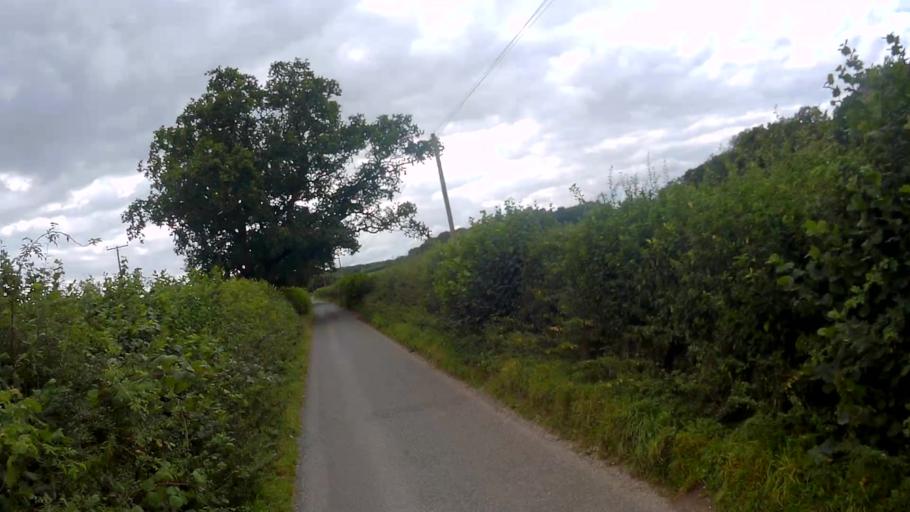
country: GB
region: England
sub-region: Hampshire
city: Overton
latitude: 51.2101
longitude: -1.2320
